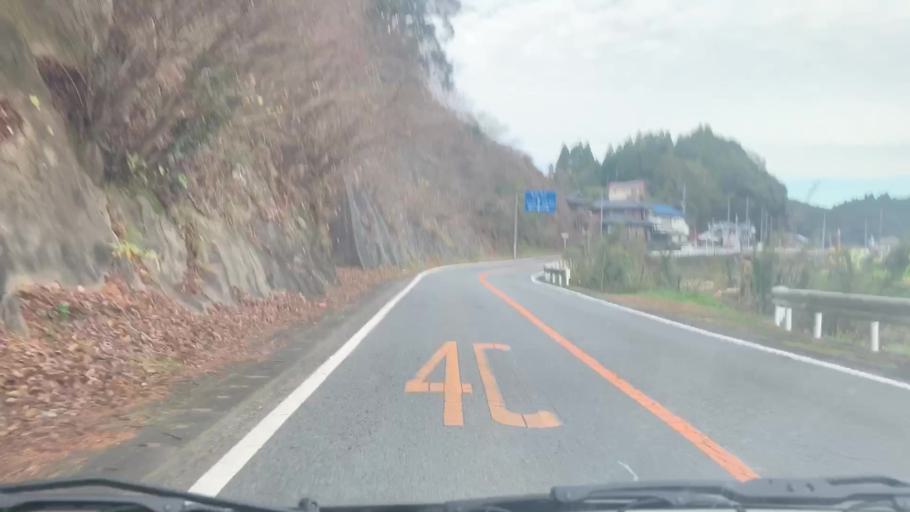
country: JP
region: Saga Prefecture
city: Takeocho-takeo
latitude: 33.2251
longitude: 129.9642
